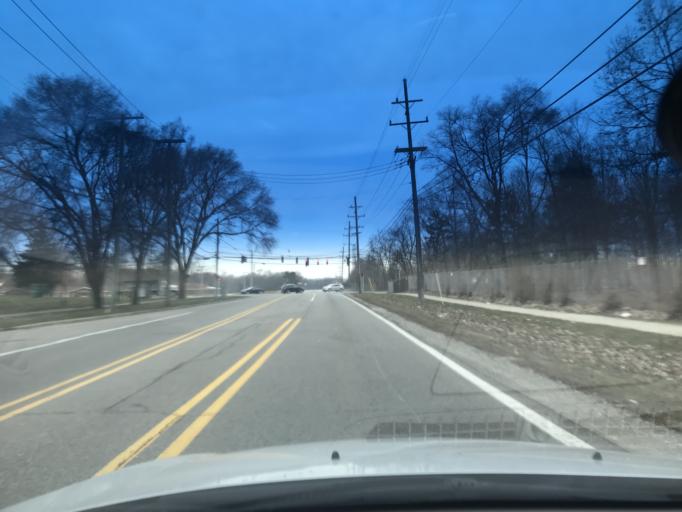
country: US
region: Michigan
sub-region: Macomb County
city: Shelby
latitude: 42.6549
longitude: -83.0488
